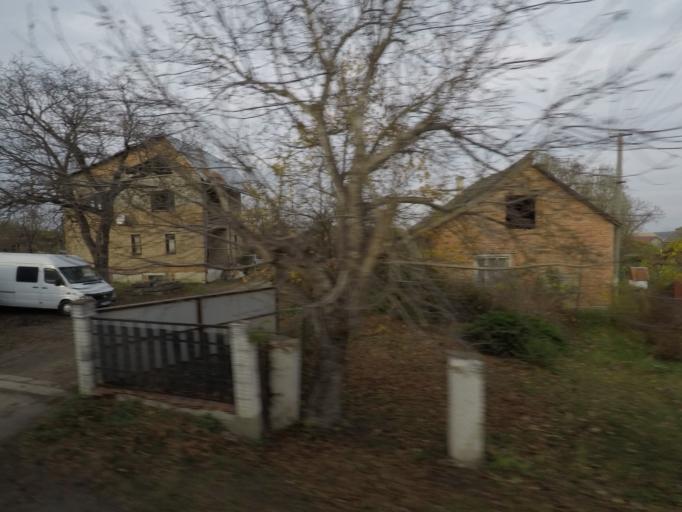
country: PL
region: Subcarpathian Voivodeship
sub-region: Powiat przemyski
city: Medyka
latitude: 49.7989
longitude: 22.9589
